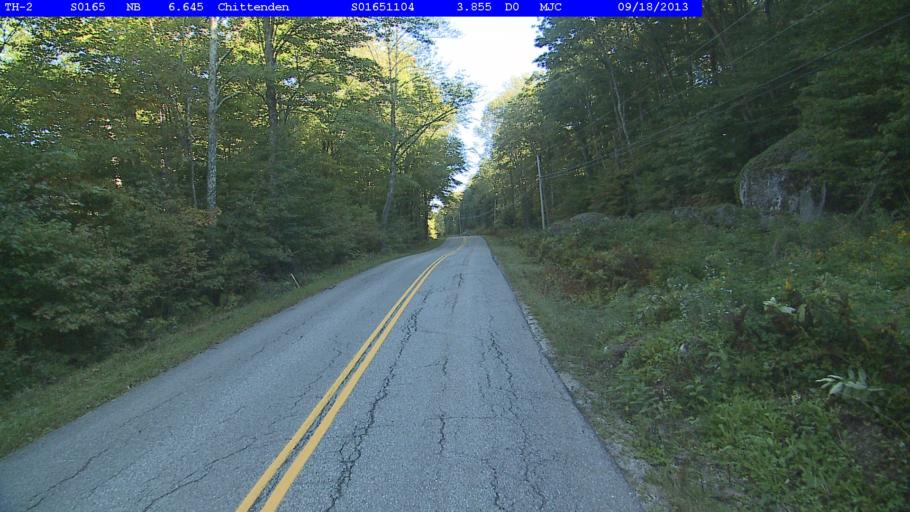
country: US
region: Vermont
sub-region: Rutland County
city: Rutland
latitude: 43.7295
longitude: -72.9708
